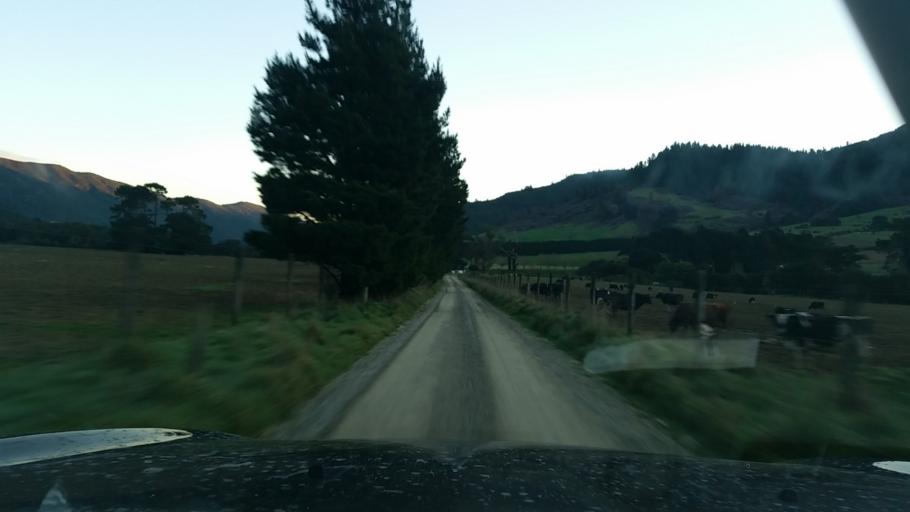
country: NZ
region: Marlborough
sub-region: Marlborough District
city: Picton
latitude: -41.1414
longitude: 174.1391
